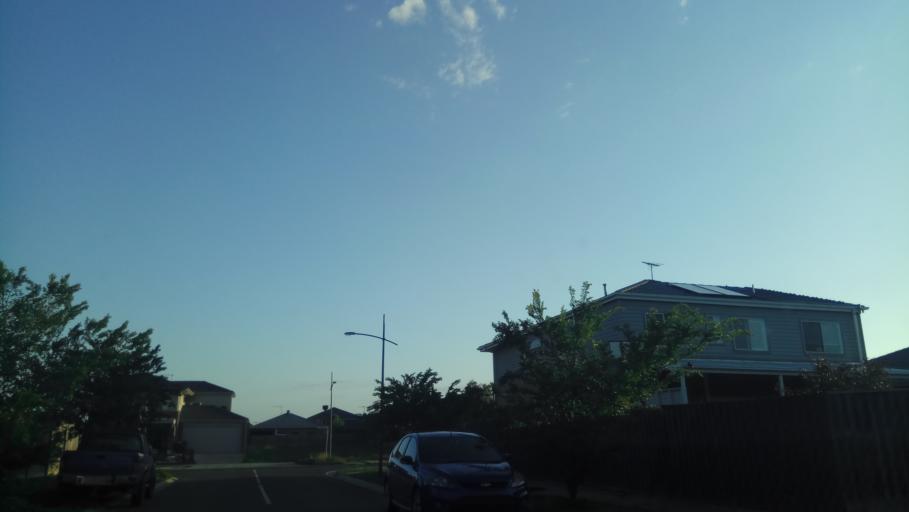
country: AU
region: Victoria
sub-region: Wyndham
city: Point Cook
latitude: -37.9062
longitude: 144.7602
